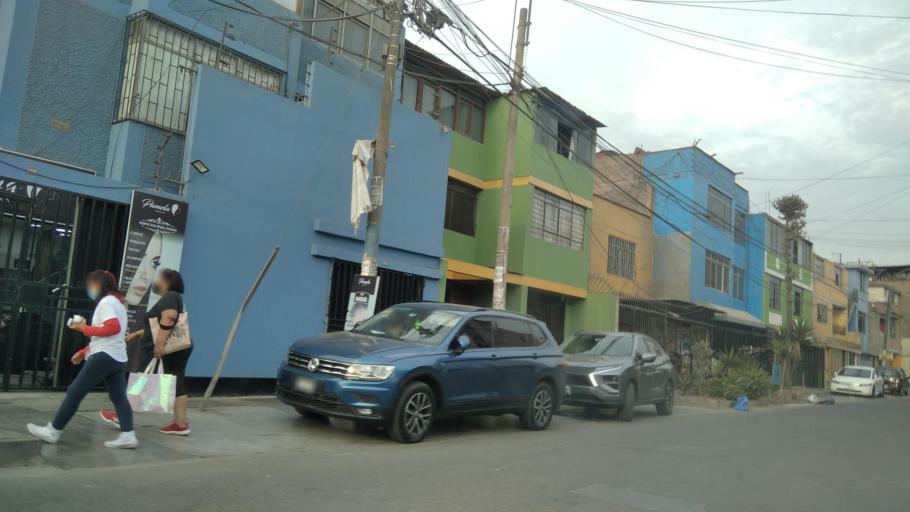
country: PE
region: Lima
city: Lima
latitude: -12.0251
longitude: -76.9964
